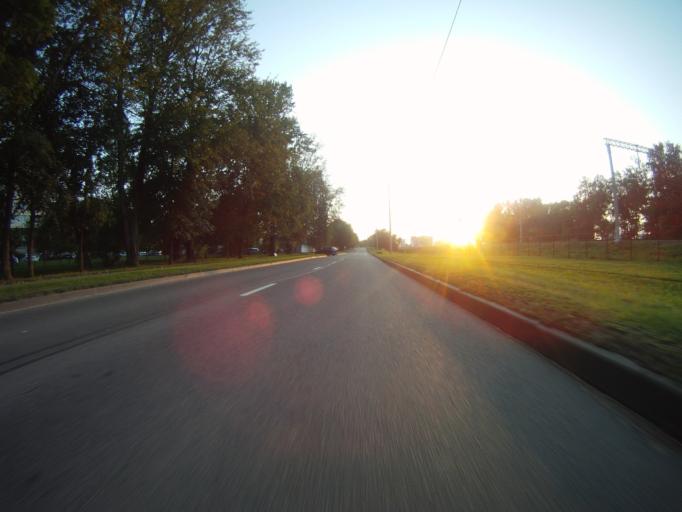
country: BY
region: Minsk
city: Zhdanovichy
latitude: 53.9304
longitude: 27.4693
